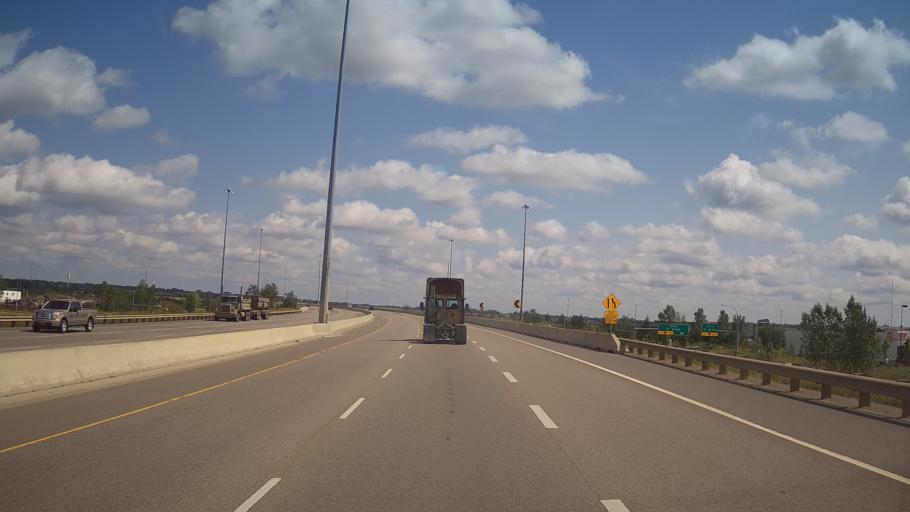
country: CA
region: Alberta
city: Sherwood Park
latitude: 53.4822
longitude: -113.3725
